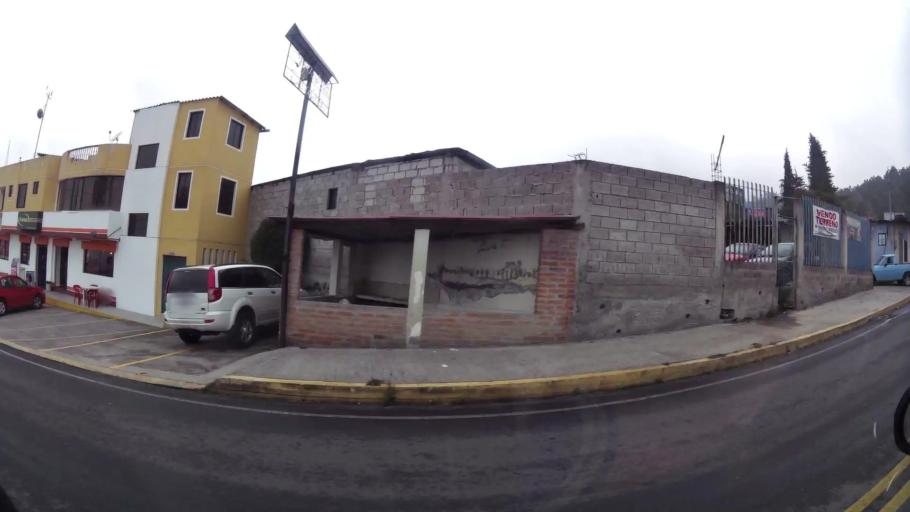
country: EC
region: Pichincha
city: Quito
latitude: -0.2626
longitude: -78.4807
